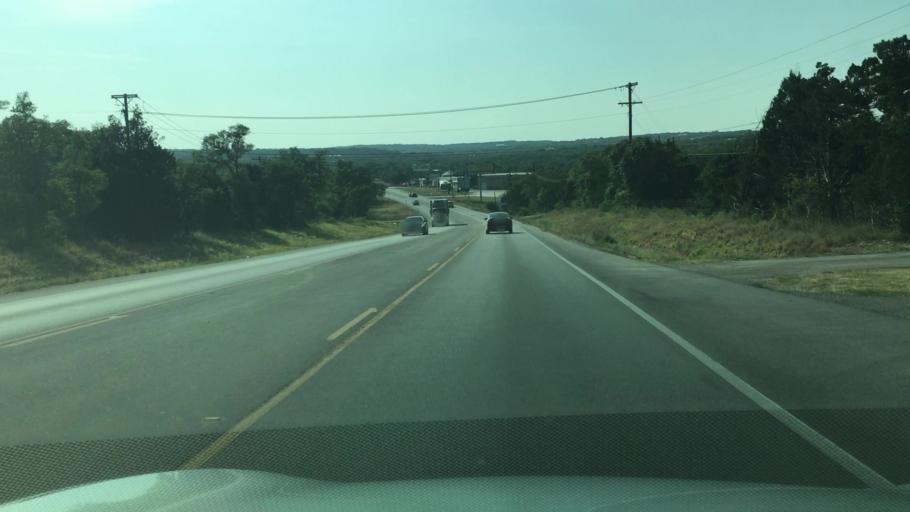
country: US
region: Texas
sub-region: Hays County
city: Wimberley
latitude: 29.9277
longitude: -98.0673
